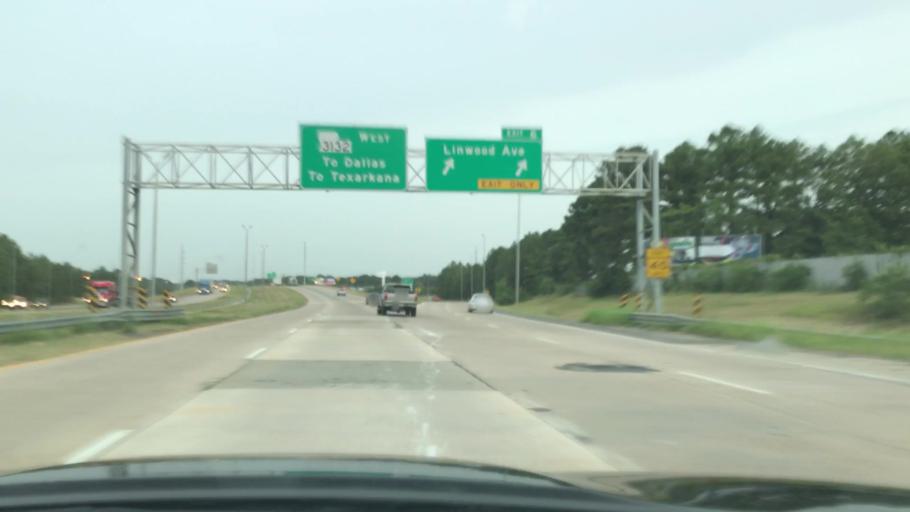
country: US
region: Louisiana
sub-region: Bossier Parish
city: Bossier City
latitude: 32.4204
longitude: -93.7580
